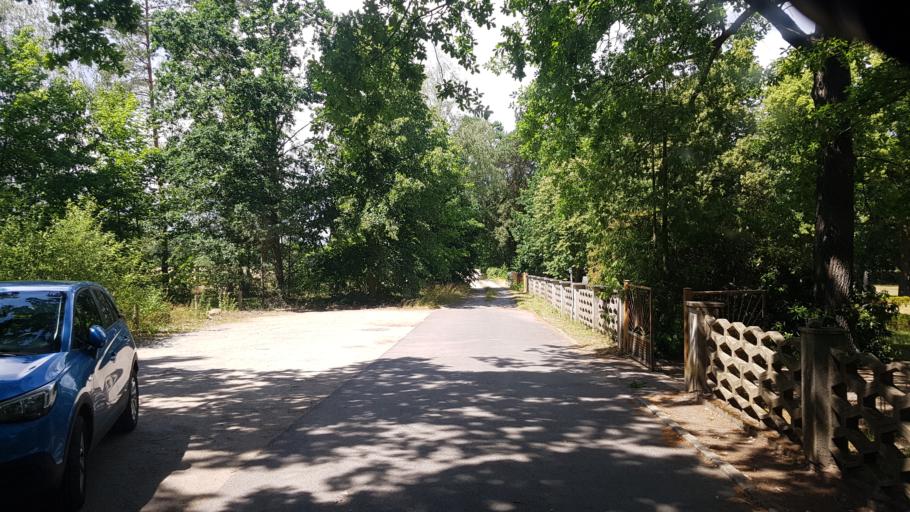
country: DE
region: Brandenburg
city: Sallgast
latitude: 51.5925
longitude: 13.8432
